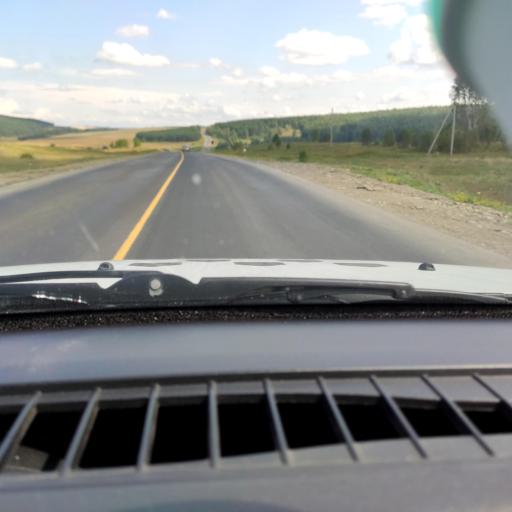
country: RU
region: Bashkortostan
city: Verkhniye Kigi
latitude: 55.3221
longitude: 58.7017
